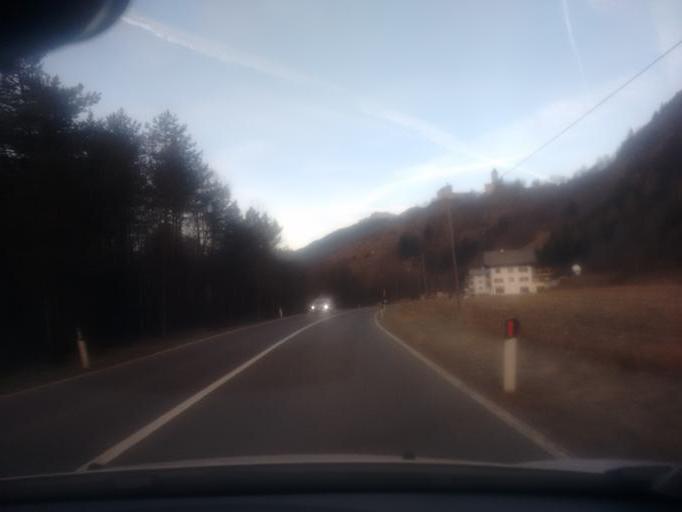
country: IT
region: Trentino-Alto Adige
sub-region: Bolzano
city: Prati
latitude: 46.8798
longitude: 11.4626
